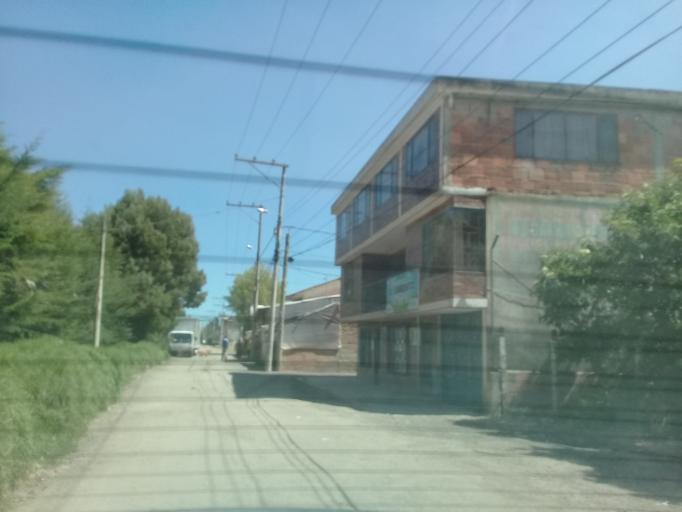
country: CO
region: Cundinamarca
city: Madrid
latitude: 4.7261
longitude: -74.2445
